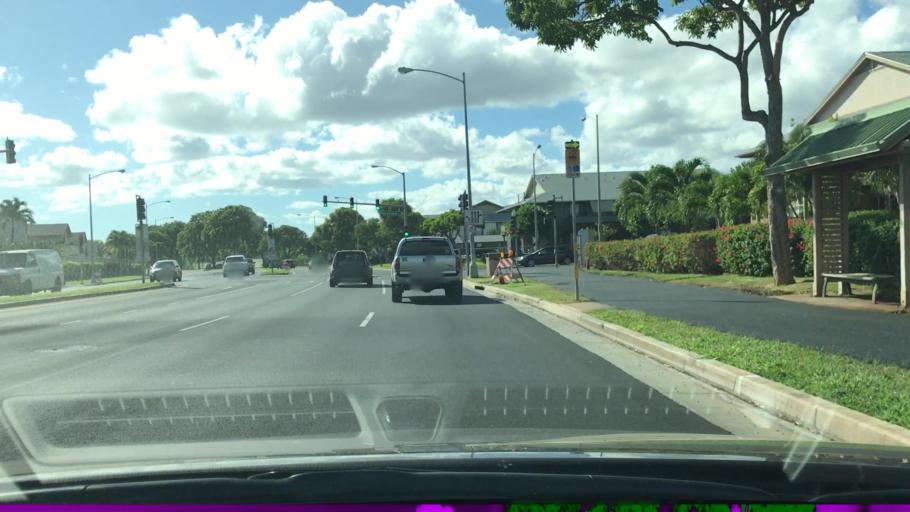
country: US
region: Hawaii
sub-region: Honolulu County
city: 'Ewa Gentry
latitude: 21.3372
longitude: -158.0317
